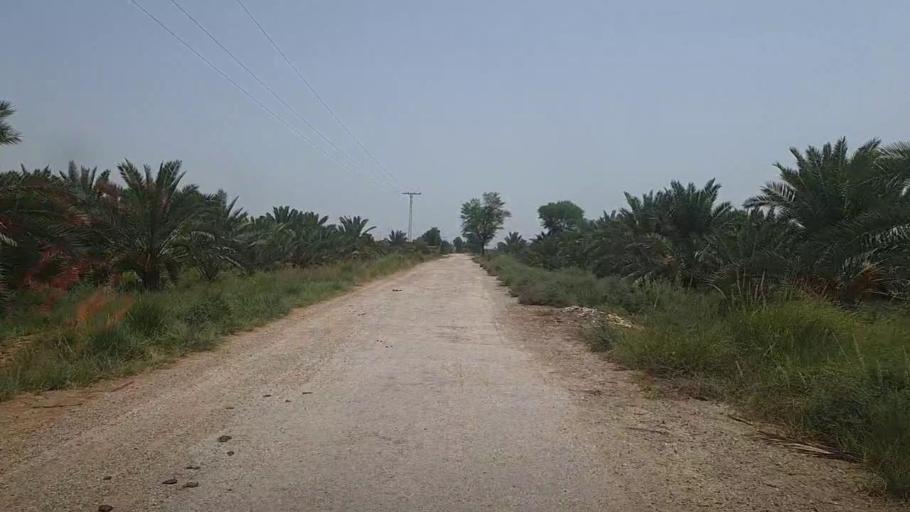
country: PK
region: Sindh
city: Pad Idan
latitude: 26.8471
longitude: 68.3247
